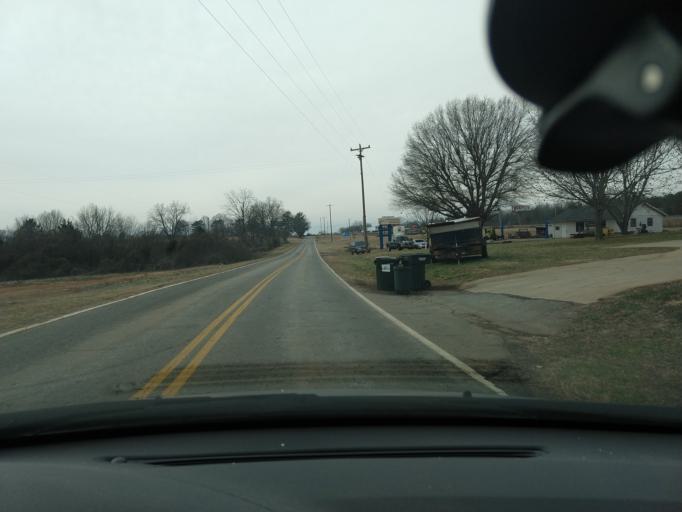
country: US
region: South Carolina
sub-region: Spartanburg County
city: Cowpens
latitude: 35.0657
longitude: -81.7678
